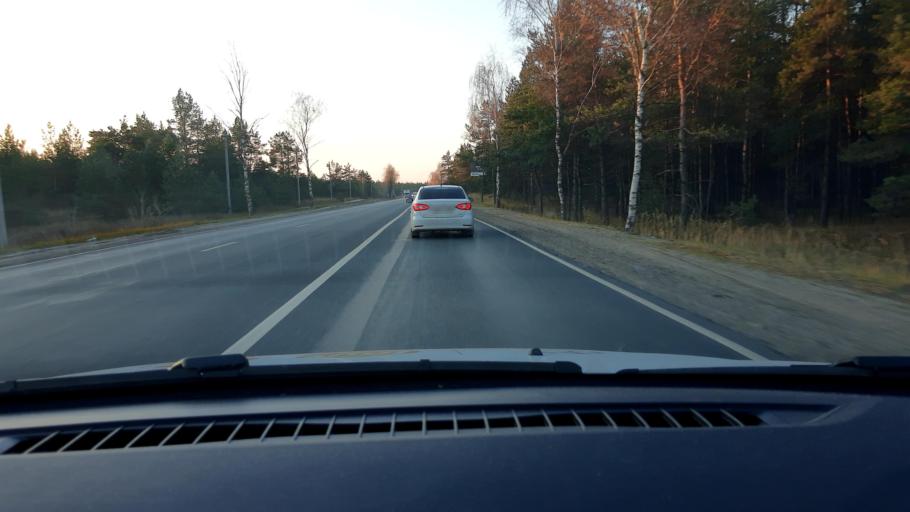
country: RU
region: Nizjnij Novgorod
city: Dzerzhinsk
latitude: 56.2815
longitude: 43.4753
